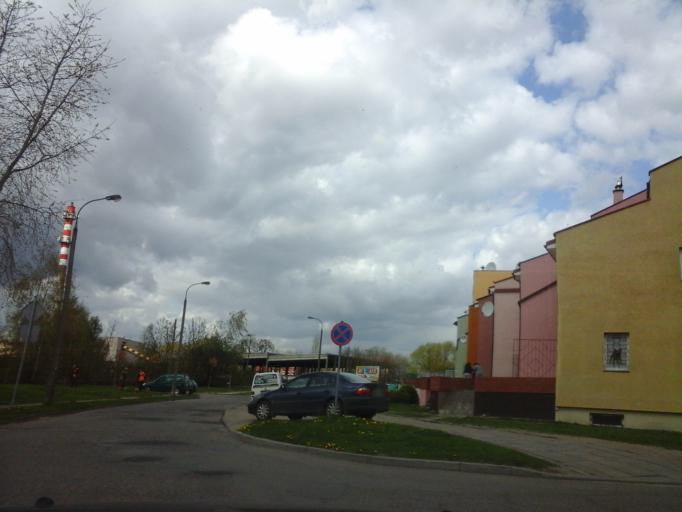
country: PL
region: West Pomeranian Voivodeship
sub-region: Powiat choszczenski
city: Choszczno
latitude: 53.1681
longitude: 15.4268
